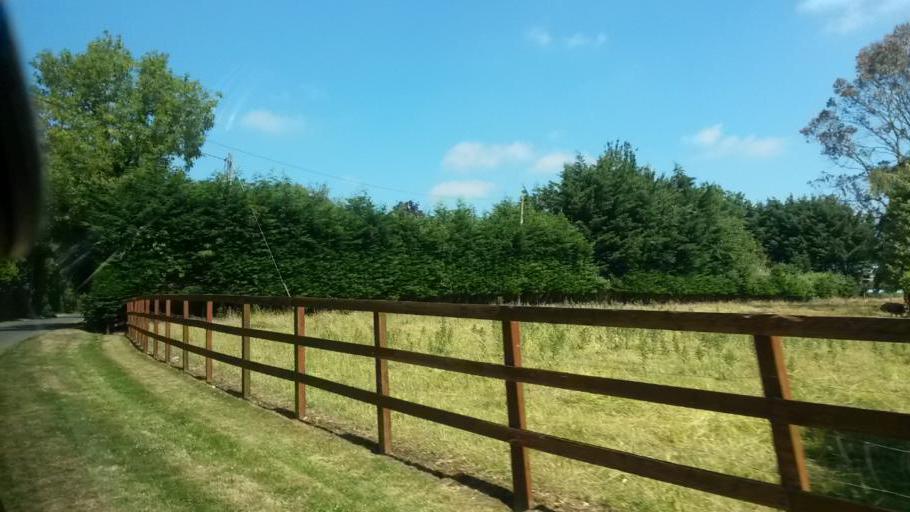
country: IE
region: Leinster
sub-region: Fingal County
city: Swords
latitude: 53.5345
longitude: -6.2504
